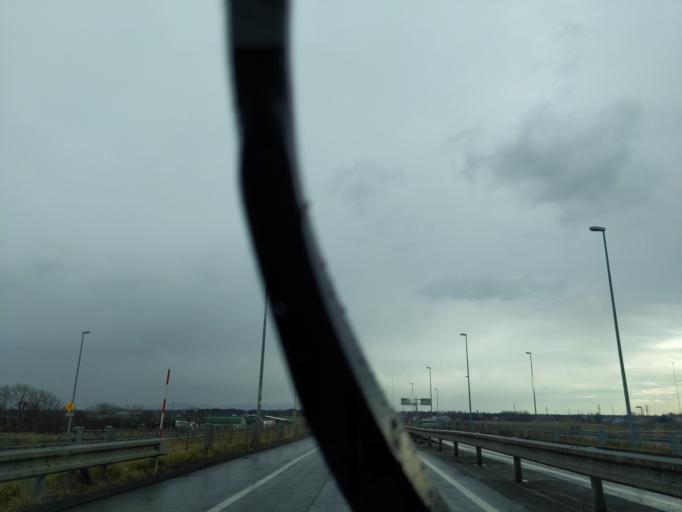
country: JP
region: Hokkaido
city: Ebetsu
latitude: 43.1149
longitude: 141.5870
